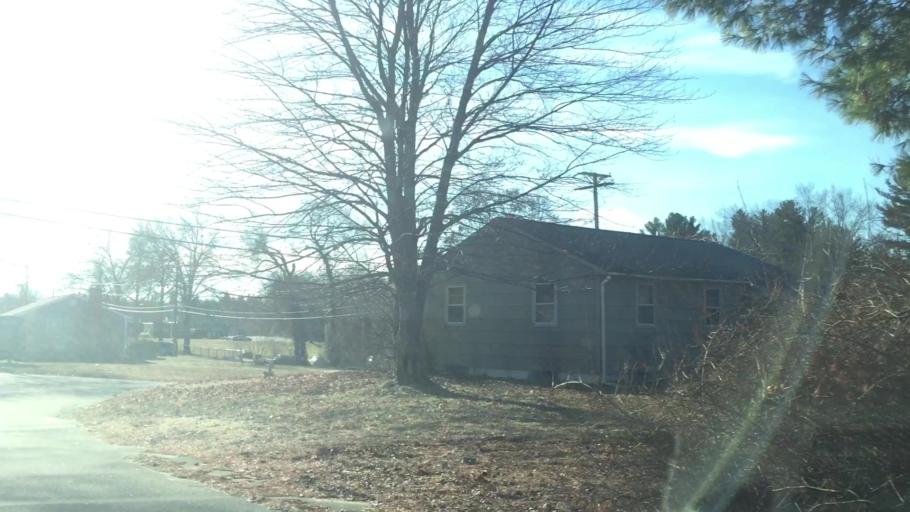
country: US
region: New Hampshire
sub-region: Rockingham County
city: Salem
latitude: 42.7857
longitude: -71.2164
